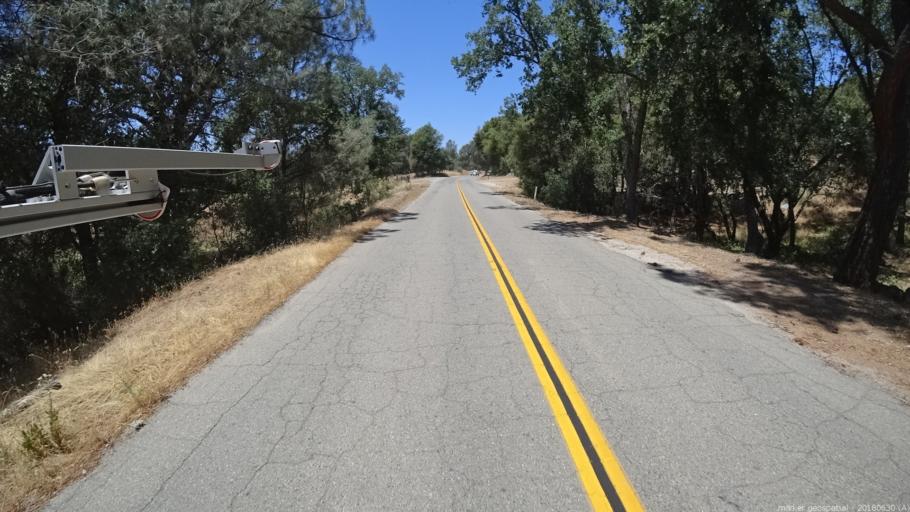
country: US
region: California
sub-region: Fresno County
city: Auberry
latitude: 37.2179
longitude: -119.4857
